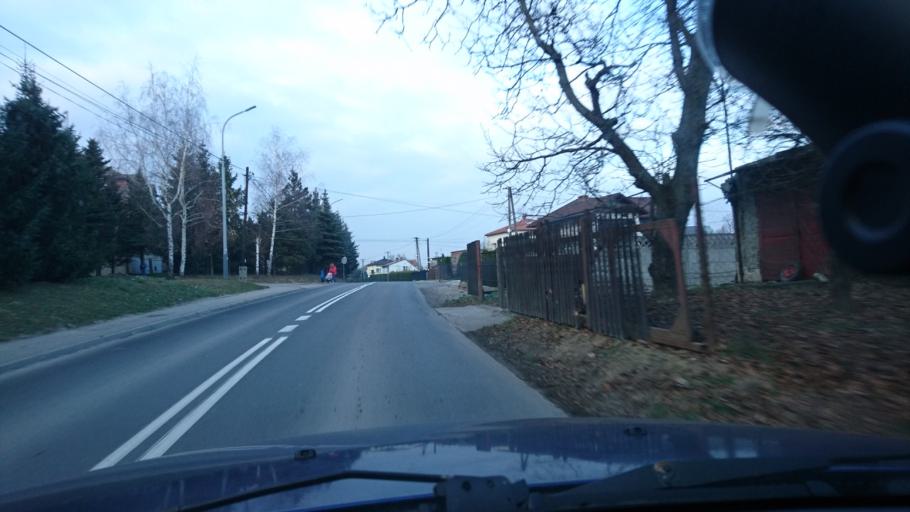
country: PL
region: Silesian Voivodeship
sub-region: Powiat bielski
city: Bestwina
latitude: 49.9003
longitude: 19.0570
